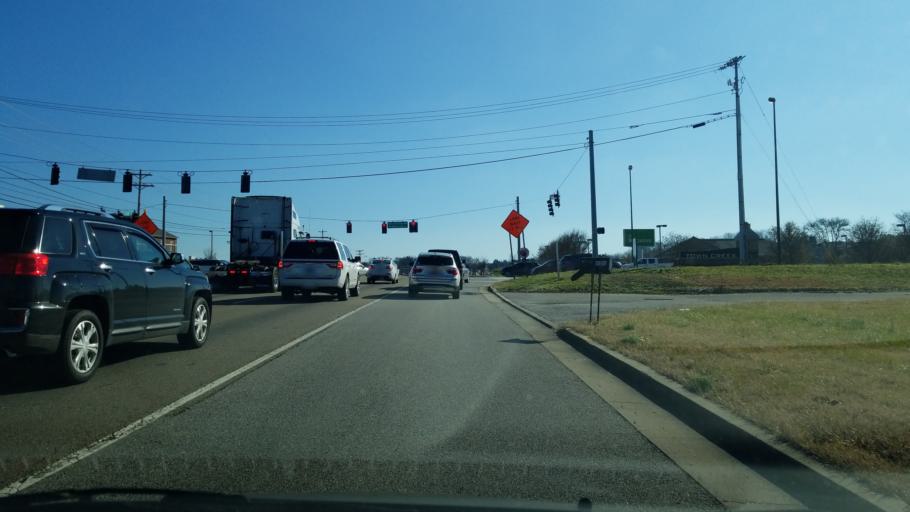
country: US
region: Tennessee
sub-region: Loudon County
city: Lenoir City
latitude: 35.8236
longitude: -84.2719
